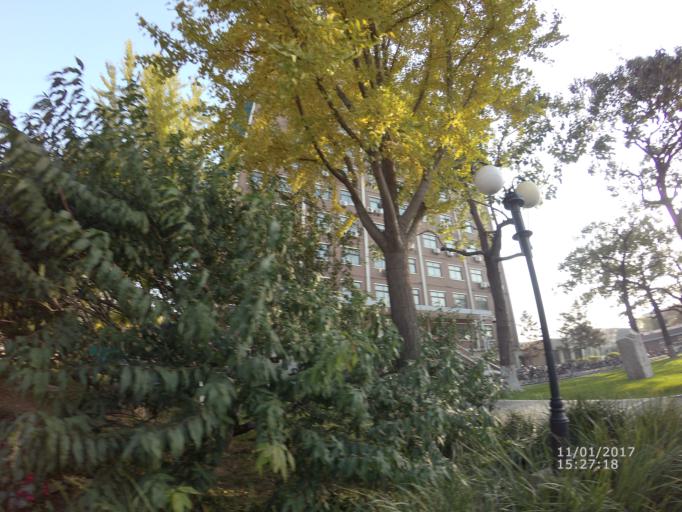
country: CN
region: Beijing
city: Xibeiwang
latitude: 40.0231
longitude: 116.2752
